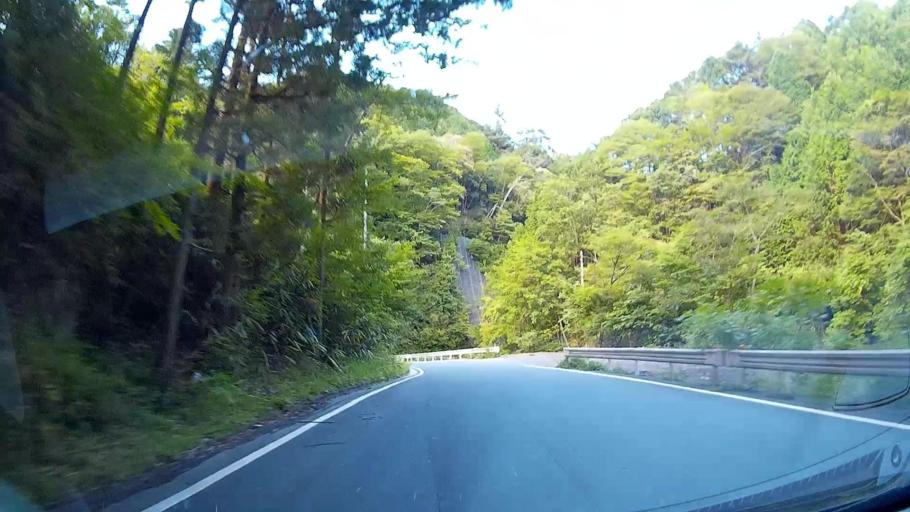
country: JP
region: Shizuoka
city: Shizuoka-shi
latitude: 35.1511
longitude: 138.2584
